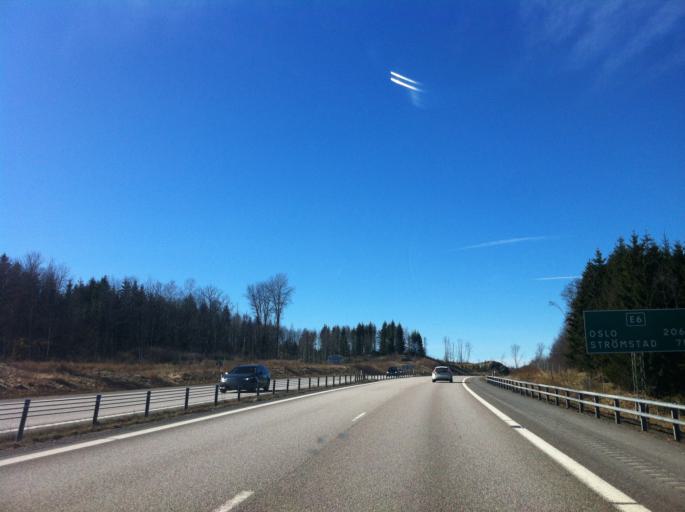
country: SE
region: Vaestra Goetaland
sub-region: Munkedals Kommun
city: Munkedal
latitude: 58.3885
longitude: 11.7639
